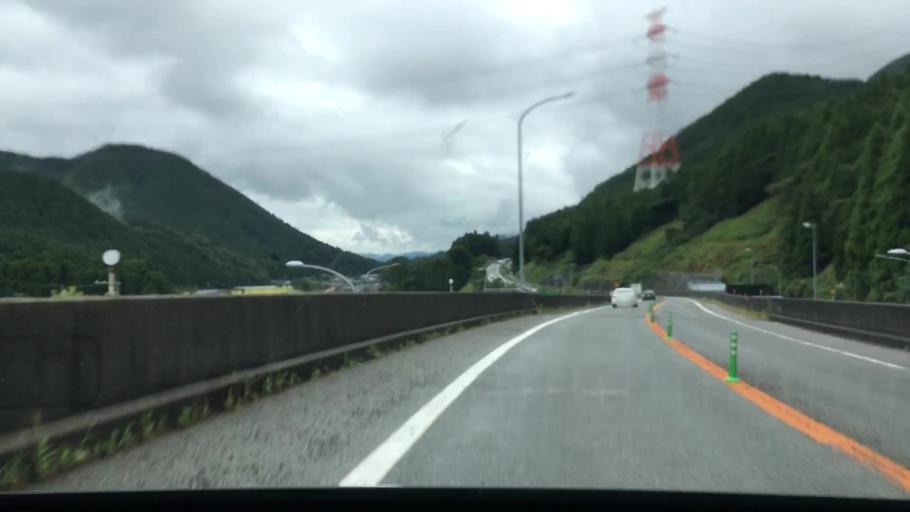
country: JP
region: Hyogo
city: Nishiwaki
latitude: 35.1189
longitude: 134.7862
